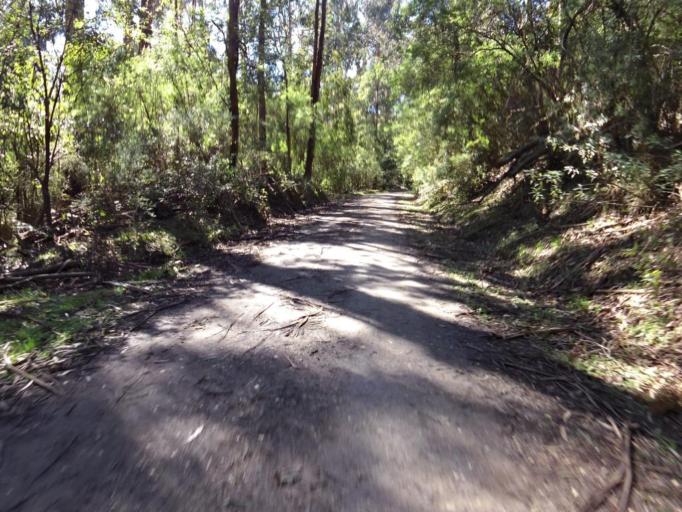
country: AU
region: Victoria
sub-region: Baw Baw
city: Warragul
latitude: -38.0661
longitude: 145.9338
